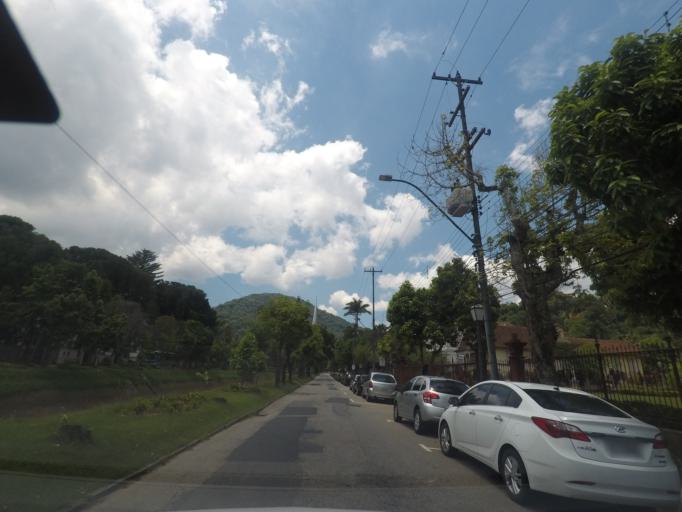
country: BR
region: Rio de Janeiro
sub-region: Petropolis
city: Petropolis
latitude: -22.5086
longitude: -43.1817
